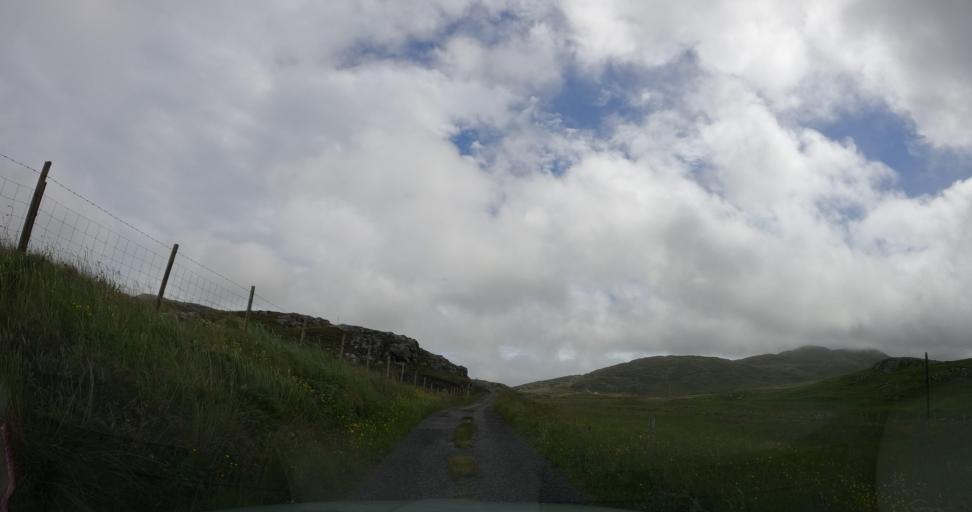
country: GB
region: Scotland
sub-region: Eilean Siar
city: Barra
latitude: 57.0040
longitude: -7.4894
